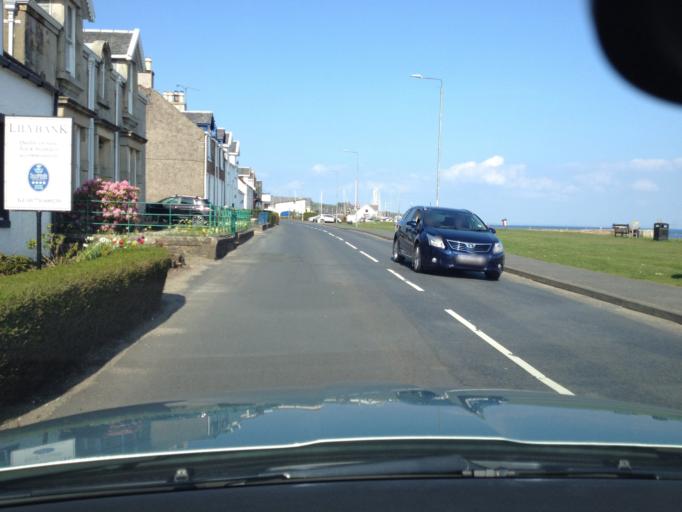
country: GB
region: Scotland
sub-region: North Ayrshire
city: Lamlash
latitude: 55.5340
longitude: -5.1273
